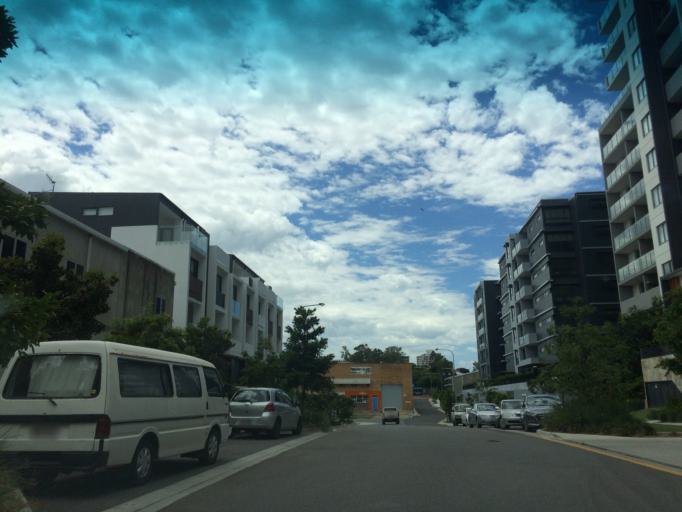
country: AU
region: Queensland
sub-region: Brisbane
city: Toowong
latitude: -27.4841
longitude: 153.0004
